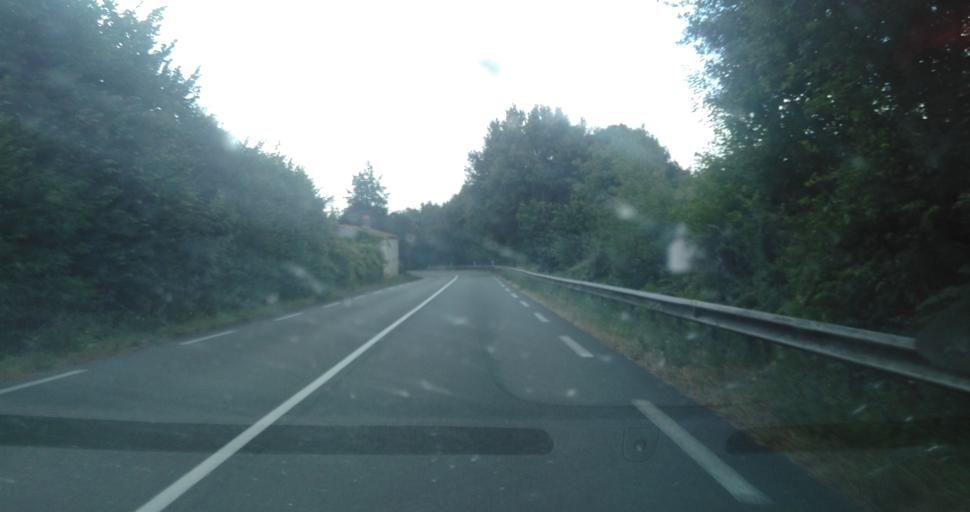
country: FR
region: Pays de la Loire
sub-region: Departement de la Vendee
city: Bournezeau
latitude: 46.5937
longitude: -1.1244
